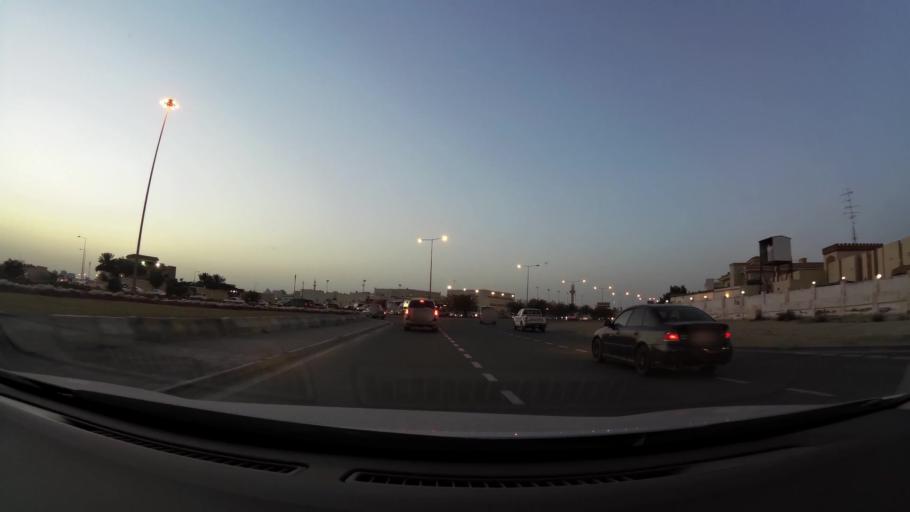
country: QA
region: Baladiyat ar Rayyan
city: Ar Rayyan
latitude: 25.3129
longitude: 51.4608
